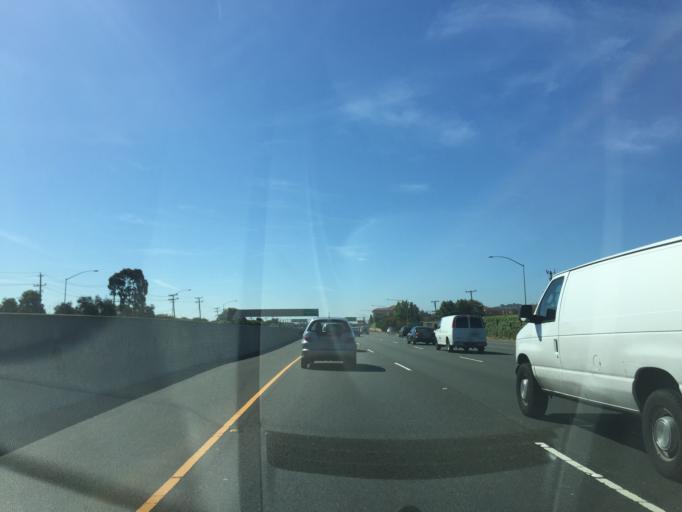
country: US
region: California
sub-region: San Mateo County
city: Foster City
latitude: 37.5509
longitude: -122.2939
